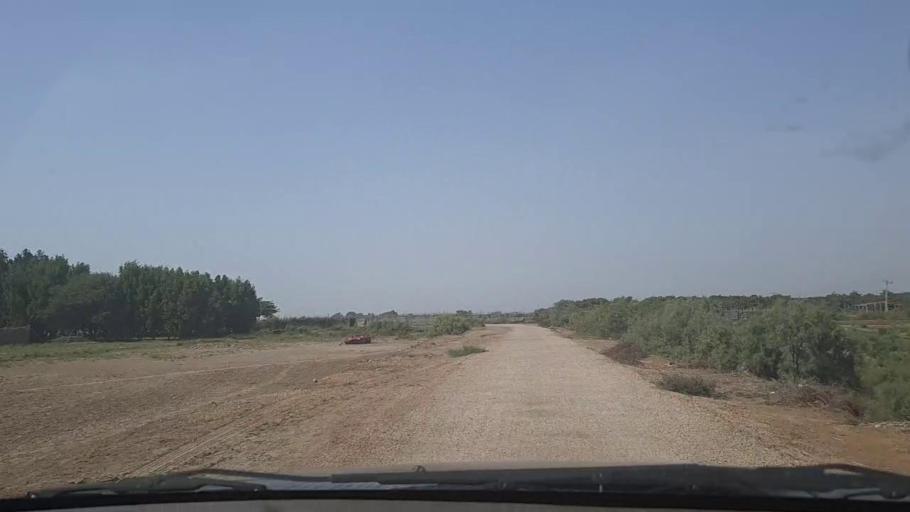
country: PK
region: Sindh
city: Keti Bandar
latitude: 24.1956
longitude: 67.5442
